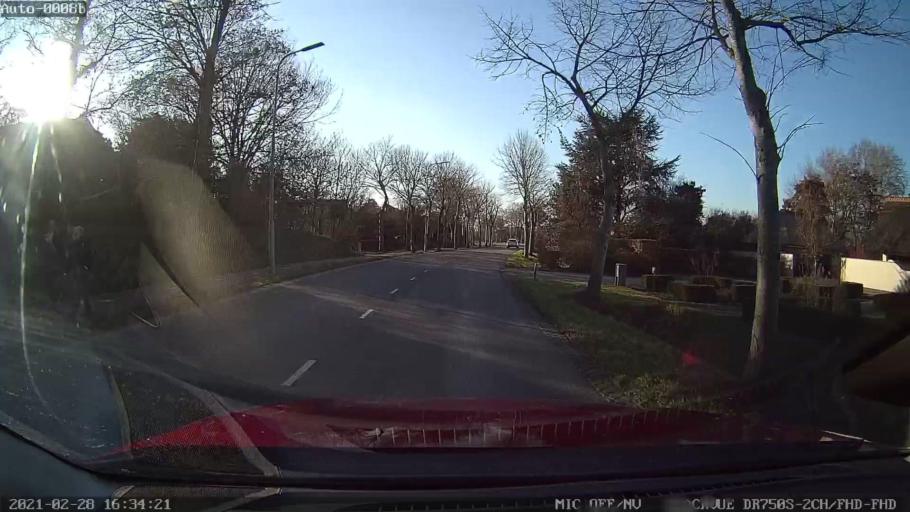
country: NL
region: Zeeland
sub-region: Gemeente Middelburg
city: Middelburg
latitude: 51.5069
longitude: 3.5926
